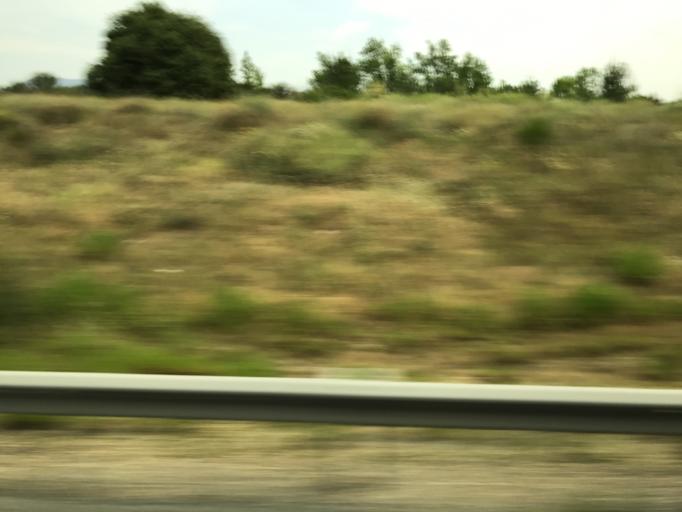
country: ES
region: Madrid
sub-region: Provincia de Madrid
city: La Cabrera
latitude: 40.9001
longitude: -3.6068
